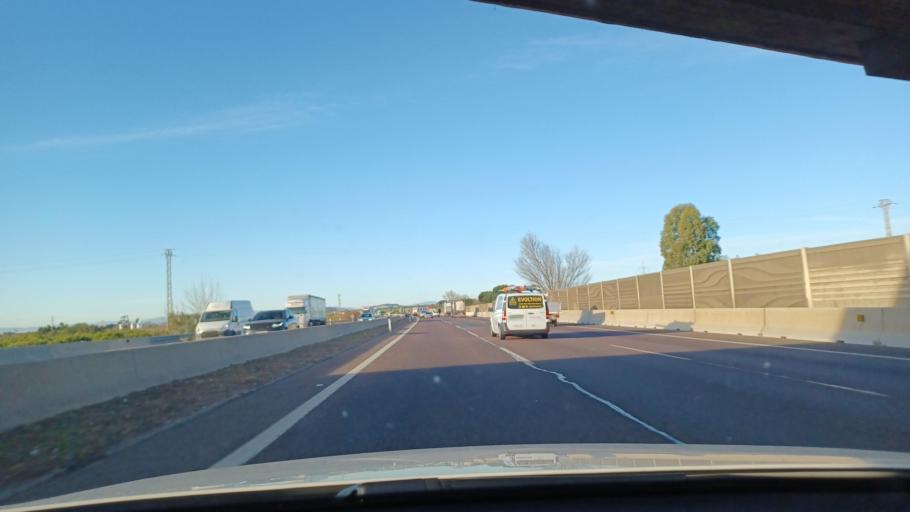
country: ES
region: Valencia
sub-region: Provincia de Valencia
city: Pucol
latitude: 39.6222
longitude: -0.3272
